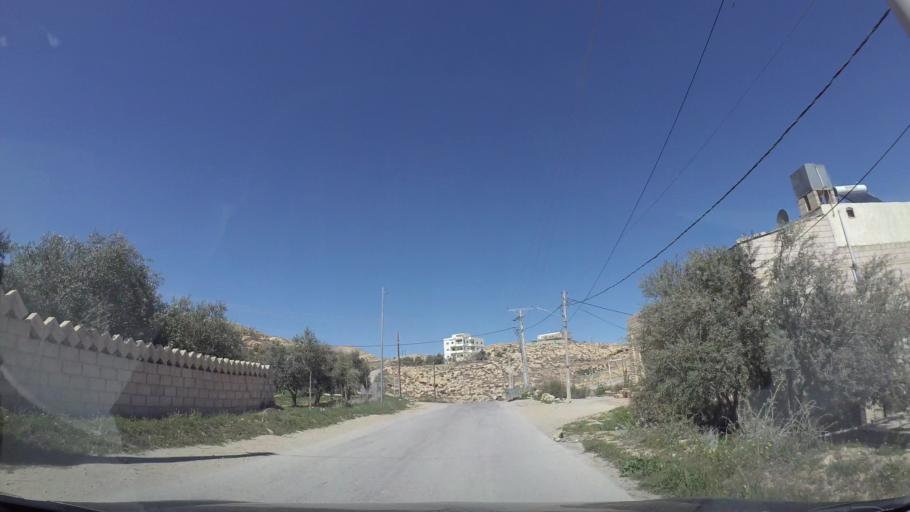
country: JO
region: Tafielah
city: At Tafilah
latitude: 30.8241
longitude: 35.5805
